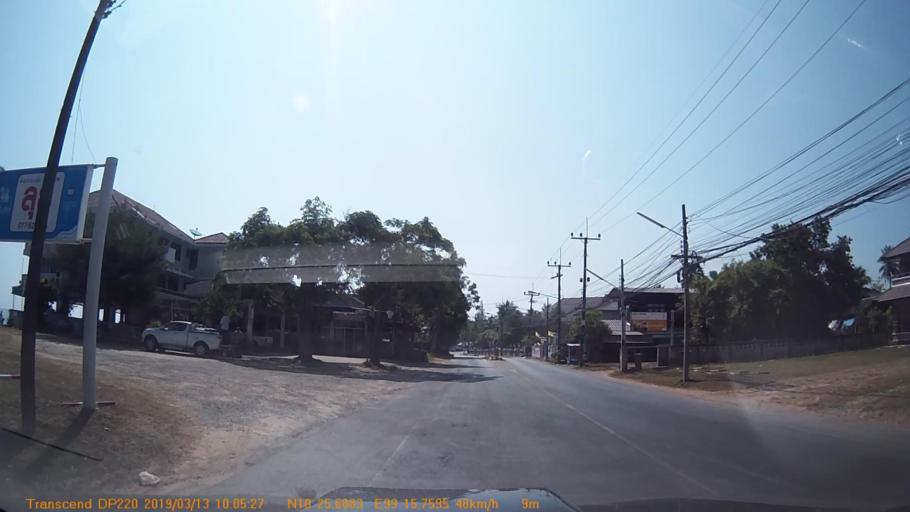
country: TH
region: Chumphon
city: Chumphon
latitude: 10.4280
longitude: 99.2628
